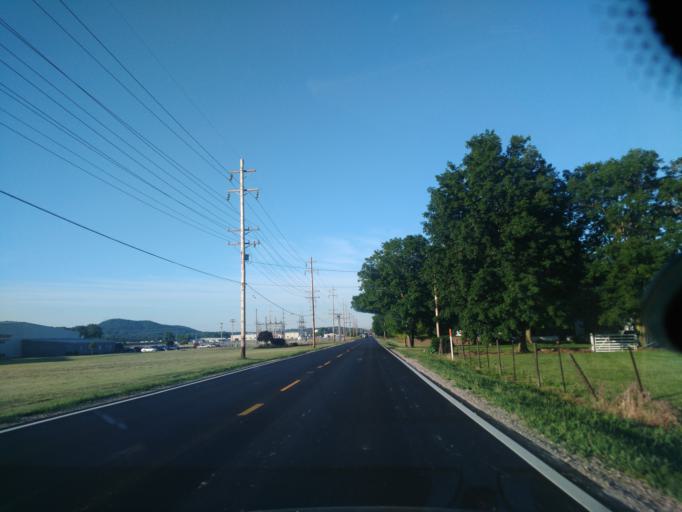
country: US
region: Ohio
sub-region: Ross County
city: Kingston
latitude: 39.4162
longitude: -82.9569
